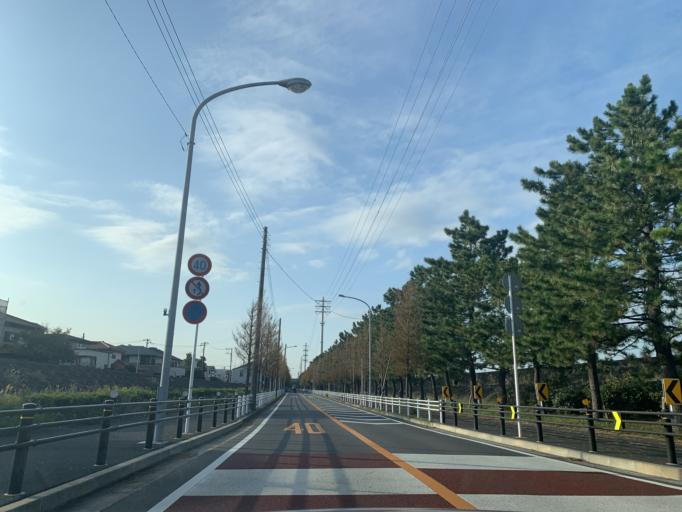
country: JP
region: Tokyo
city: Urayasu
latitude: 35.6518
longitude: 139.9233
